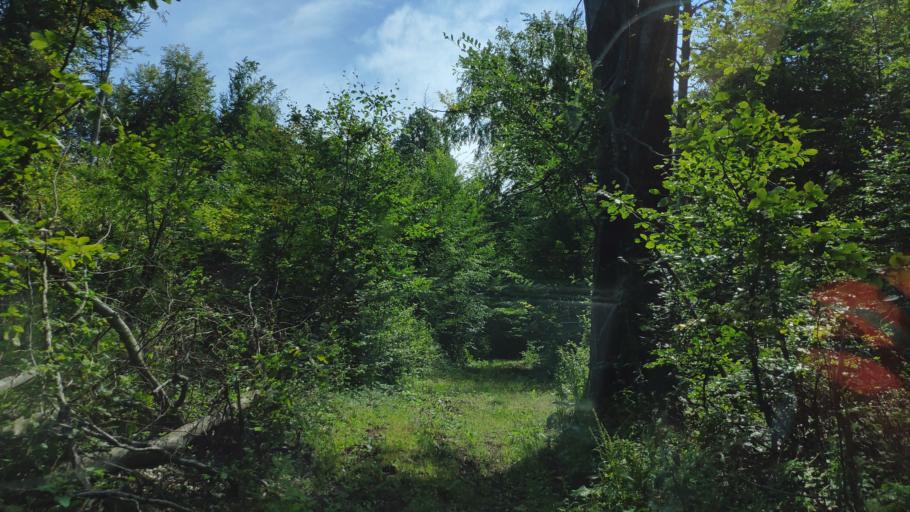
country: SK
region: Kosicky
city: Dobsina
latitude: 48.7108
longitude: 20.3883
